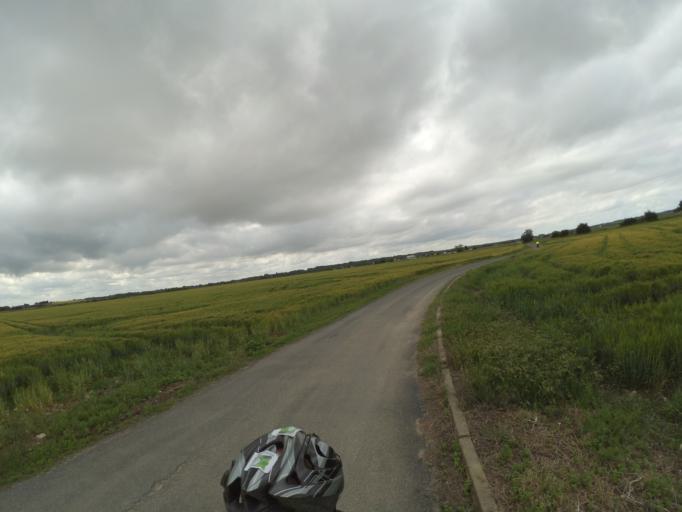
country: FR
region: Poitou-Charentes
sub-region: Departement de la Charente-Maritime
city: Yves
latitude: 46.0110
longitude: -1.0463
